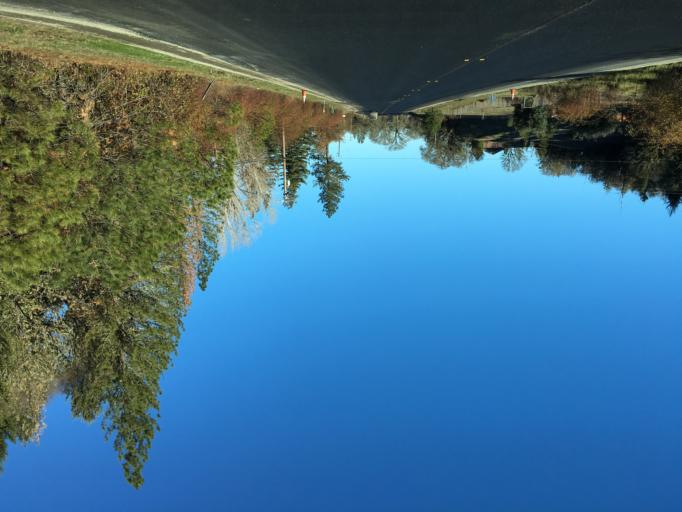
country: US
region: California
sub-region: Mendocino County
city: Laytonville
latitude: 39.6378
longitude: -123.4699
